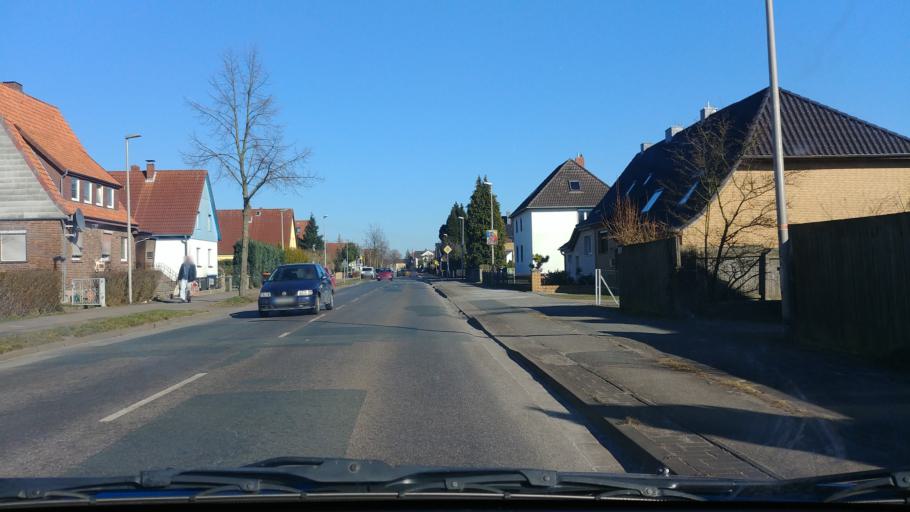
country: DE
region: Lower Saxony
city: Neustadt am Rubenberge
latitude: 52.5045
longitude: 9.4414
